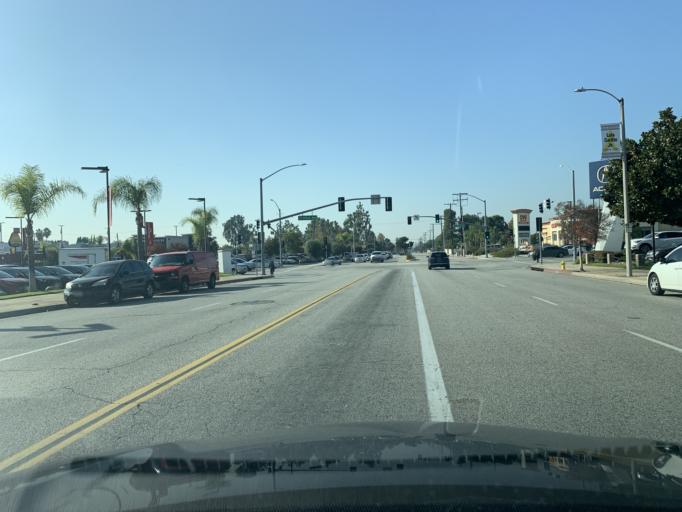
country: US
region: California
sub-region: Los Angeles County
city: Covina
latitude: 34.0790
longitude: -117.8894
